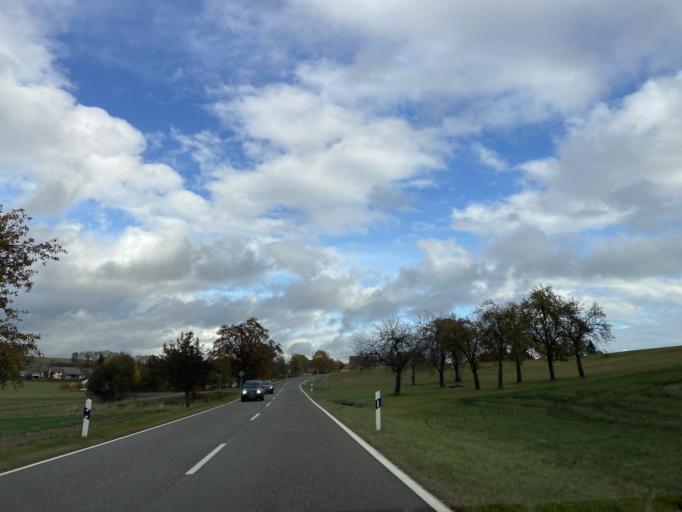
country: DE
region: Baden-Wuerttemberg
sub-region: Tuebingen Region
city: Leibertingen
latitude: 48.0556
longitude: 9.0265
